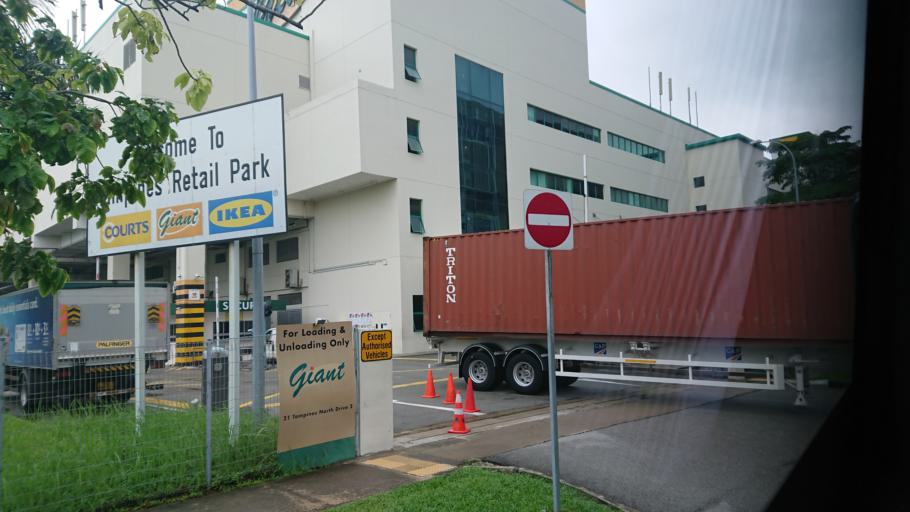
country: MY
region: Johor
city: Kampung Pasir Gudang Baru
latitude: 1.3712
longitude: 103.9328
